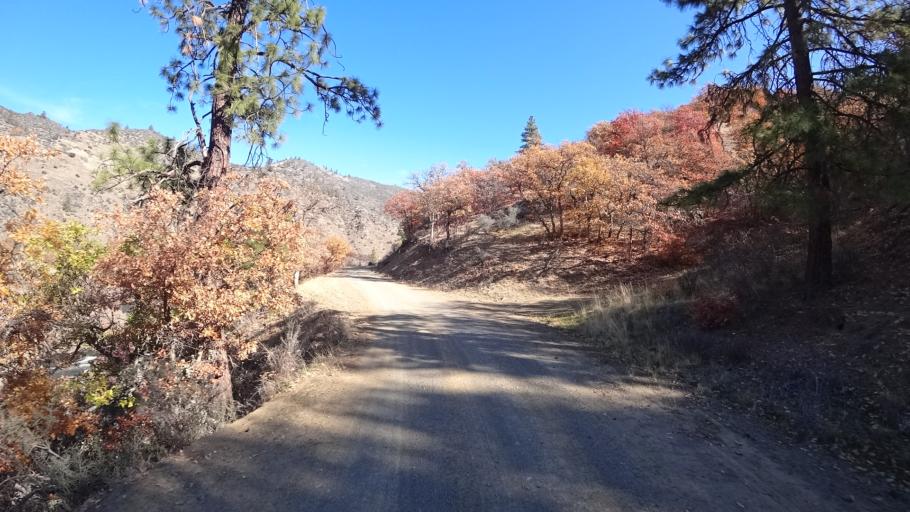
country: US
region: California
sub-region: Siskiyou County
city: Yreka
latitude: 41.8630
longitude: -122.7136
